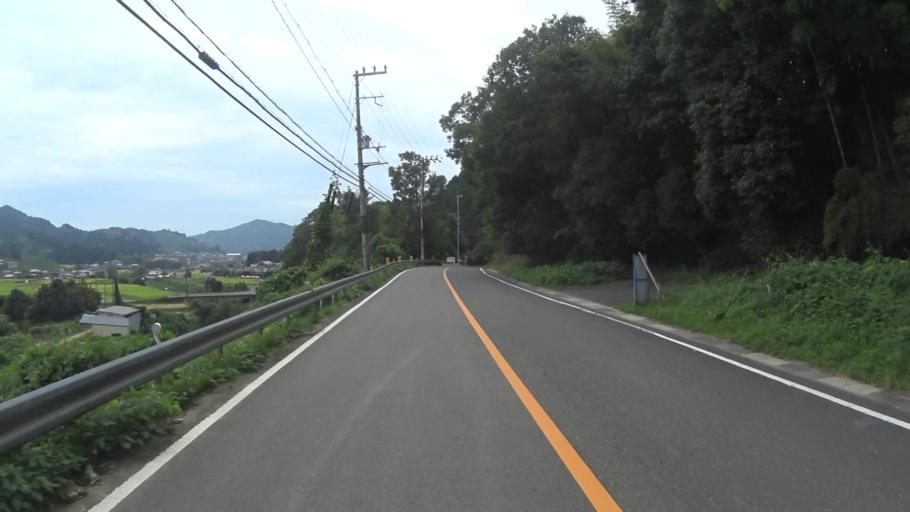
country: JP
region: Kyoto
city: Uji
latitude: 34.8120
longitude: 135.9174
